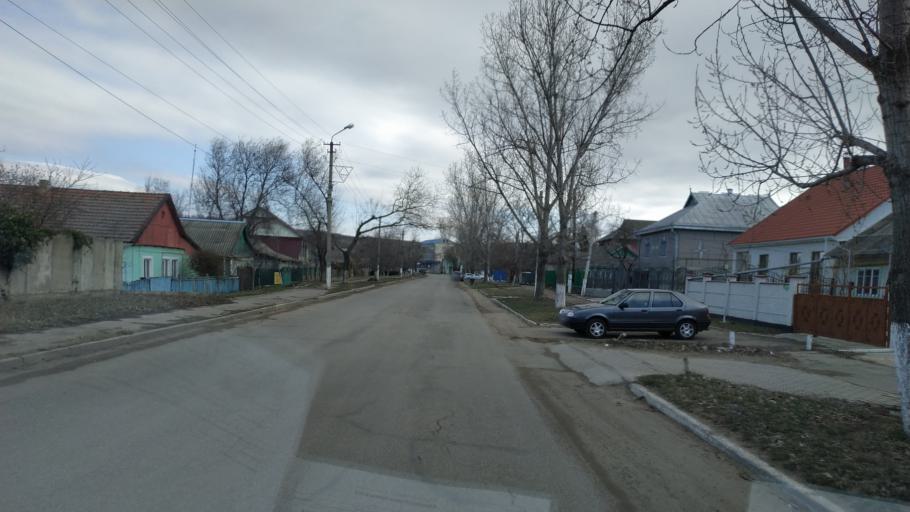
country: MD
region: Causeni
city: Causeni
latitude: 46.6413
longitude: 29.4001
